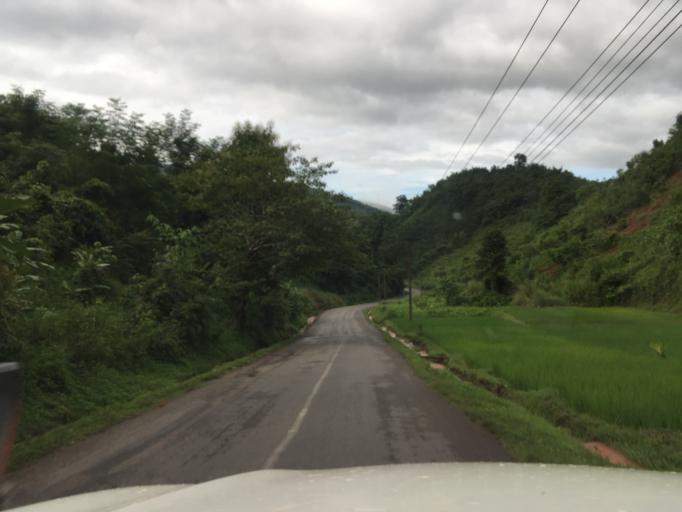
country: LA
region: Oudomxai
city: Muang La
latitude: 20.7989
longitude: 102.0862
